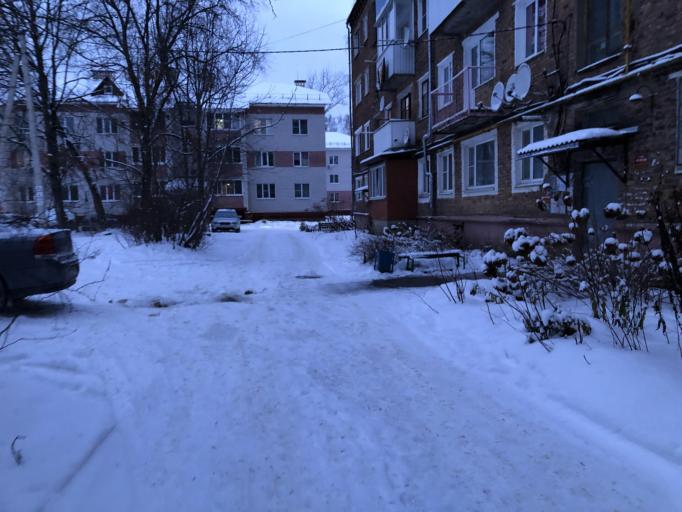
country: RU
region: Smolensk
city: Safonovo
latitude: 55.1153
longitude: 33.2348
